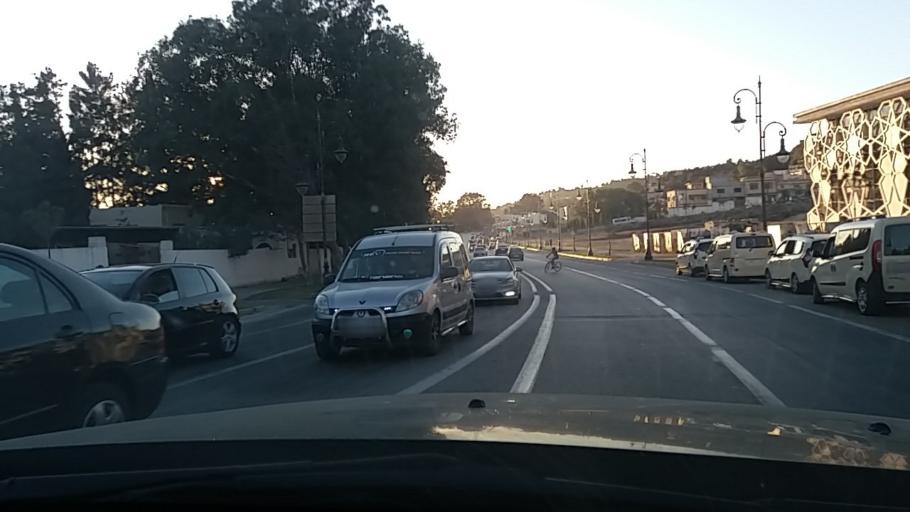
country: MA
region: Tanger-Tetouan
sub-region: Tanger-Assilah
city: Boukhalef
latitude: 35.7389
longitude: -5.8756
